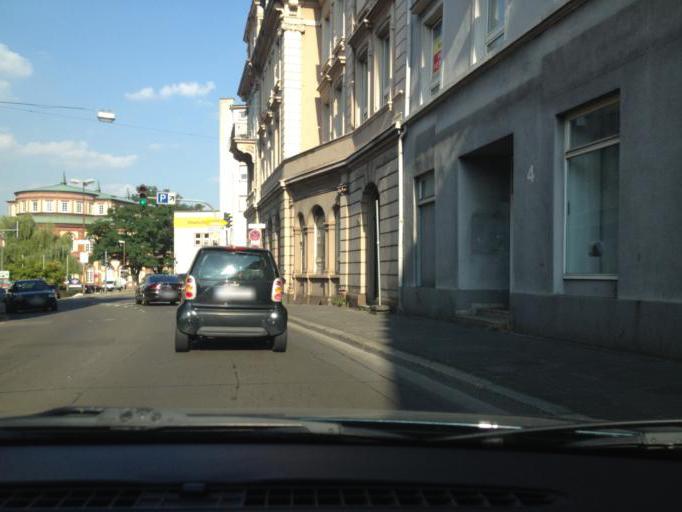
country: DE
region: Rheinland-Pfalz
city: Neustadt
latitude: 49.3501
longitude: 8.1374
